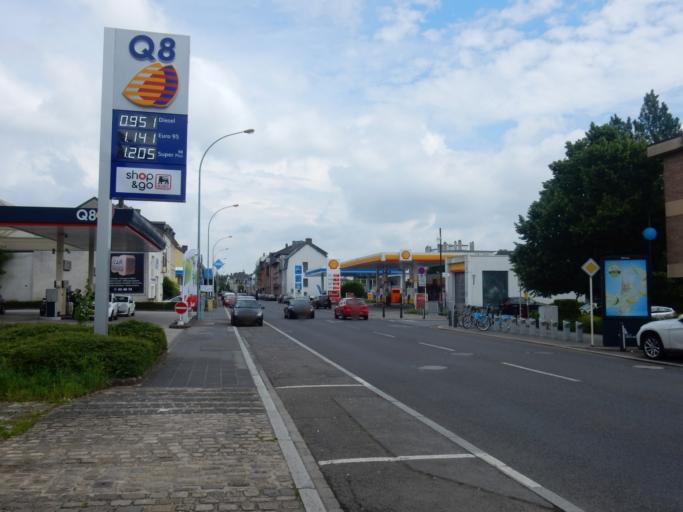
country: LU
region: Luxembourg
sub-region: Canton de Luxembourg
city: Strassen
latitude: 49.6056
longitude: 6.0999
